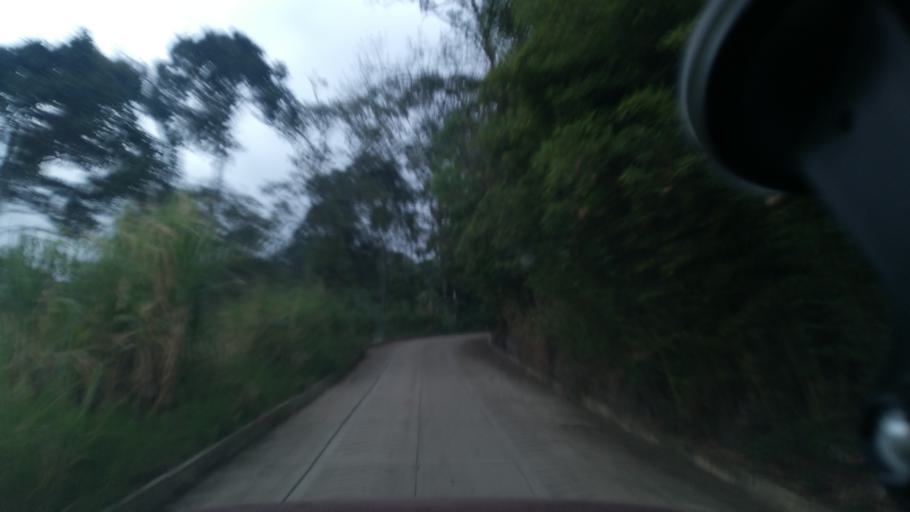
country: CO
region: Cundinamarca
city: San Antonio del Tequendama
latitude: 4.6619
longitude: -74.3984
